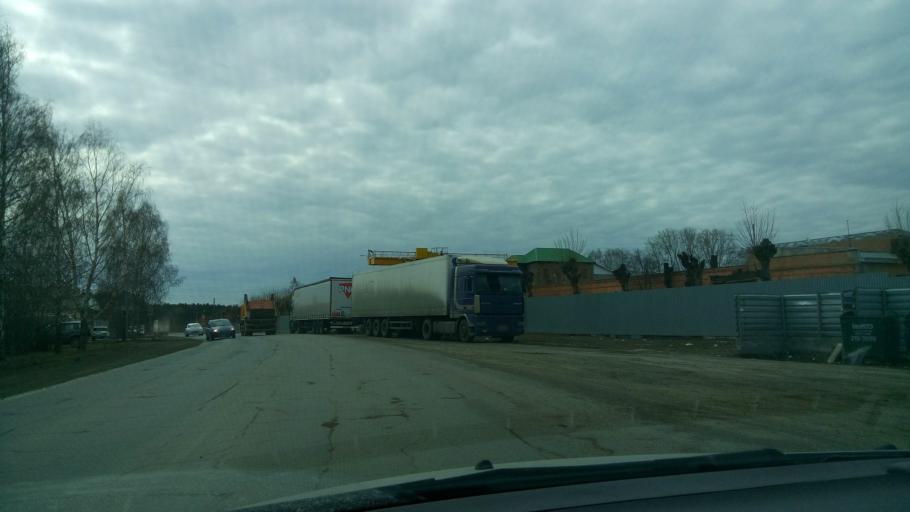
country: RU
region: Sverdlovsk
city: Verkhnyaya Pyshma
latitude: 56.9558
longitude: 60.6673
